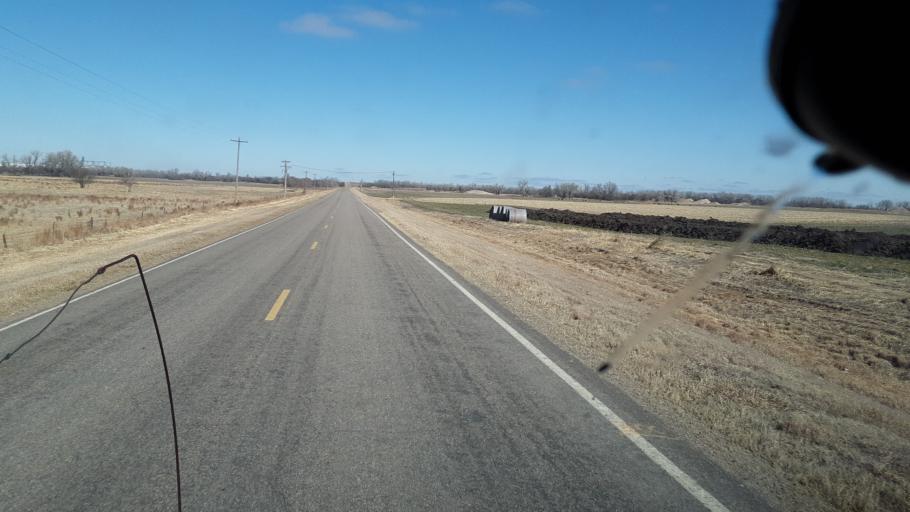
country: US
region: Kansas
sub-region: Barton County
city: Ellinwood
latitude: 38.3415
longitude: -98.6643
